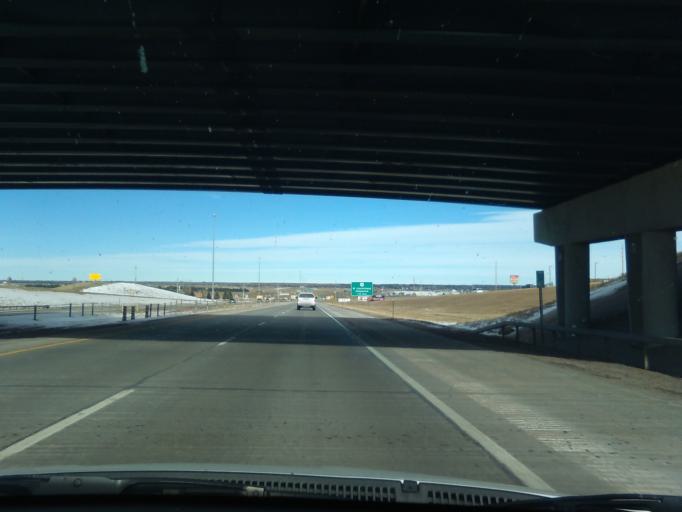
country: US
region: Wyoming
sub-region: Laramie County
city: South Greeley
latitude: 41.0994
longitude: -104.8503
